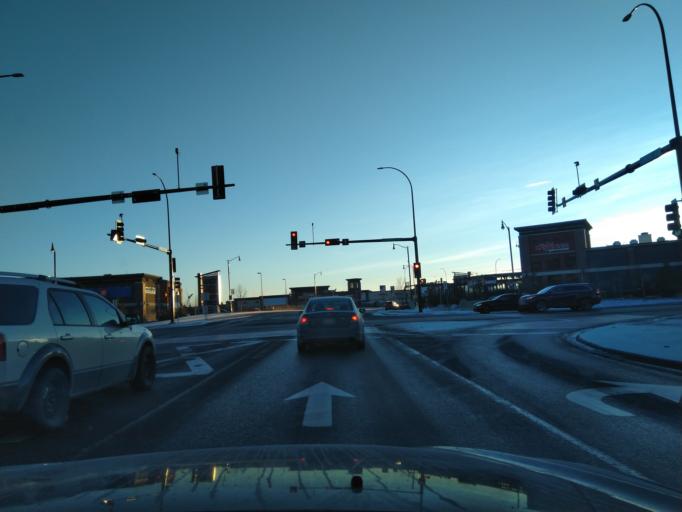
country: CA
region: Alberta
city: Cochrane
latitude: 51.1880
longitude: -114.4675
